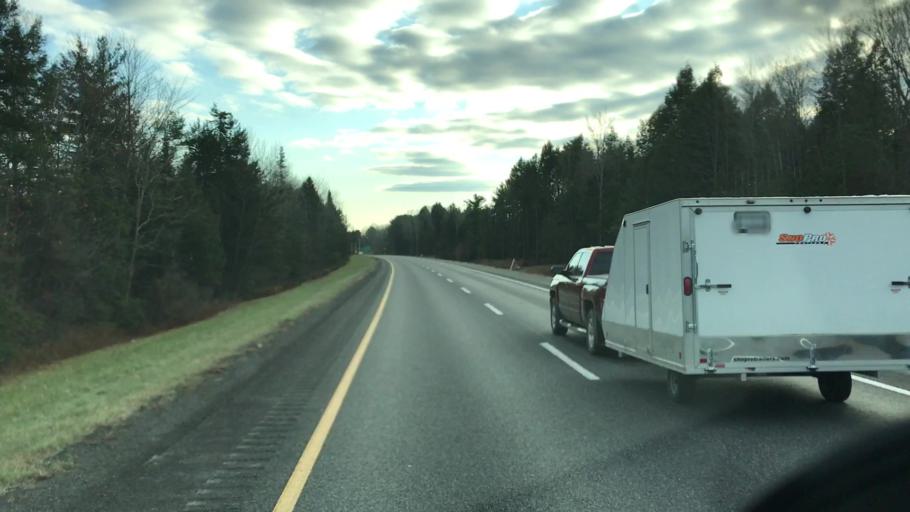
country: US
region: Maine
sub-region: Kennebec County
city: Oakland
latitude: 44.5146
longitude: -69.7024
